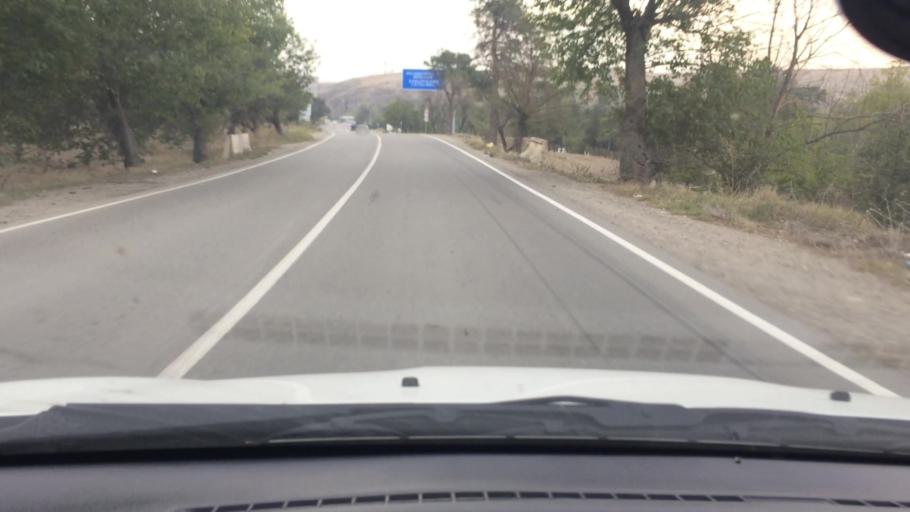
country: GE
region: Kvemo Kartli
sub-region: Gardabani
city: Gardabani
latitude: 41.3377
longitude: 45.0689
